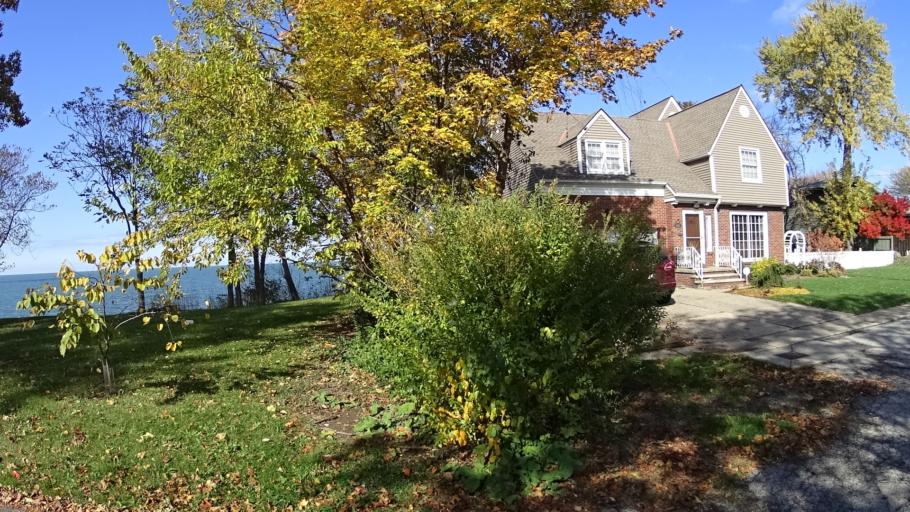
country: US
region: Ohio
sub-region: Lorain County
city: Lorain
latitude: 41.4592
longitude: -82.2035
